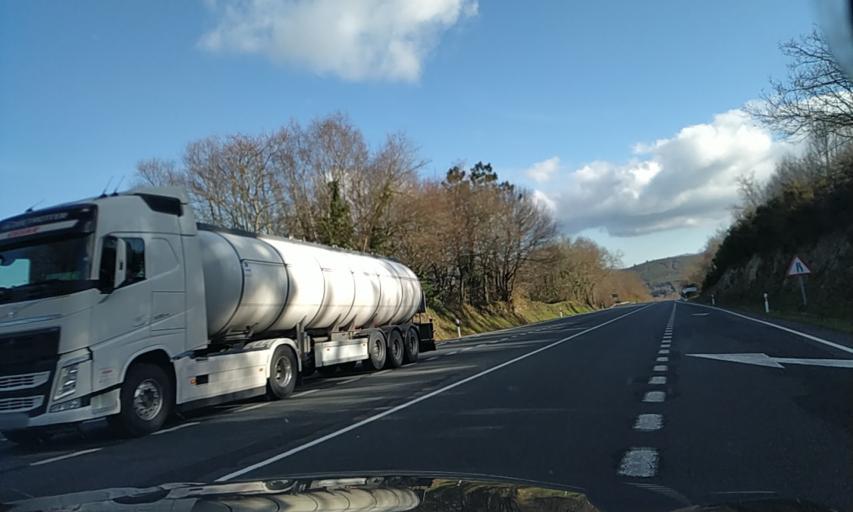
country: ES
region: Galicia
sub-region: Provincia de Pontevedra
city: Silleda
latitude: 42.7050
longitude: -8.3441
